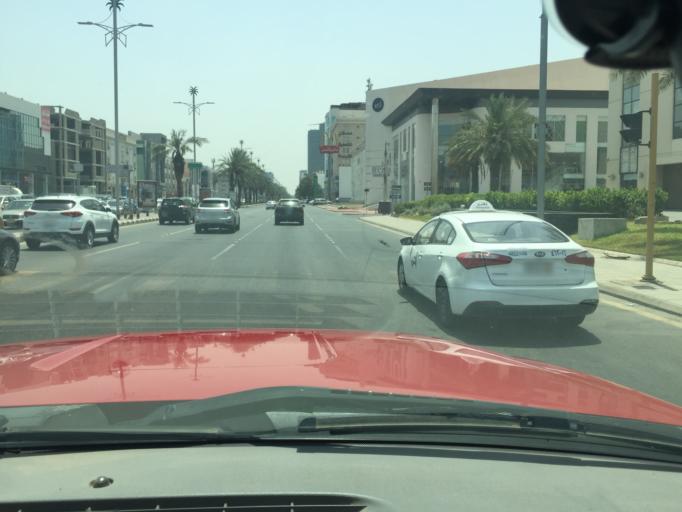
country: SA
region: Makkah
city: Jeddah
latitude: 21.5503
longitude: 39.1550
